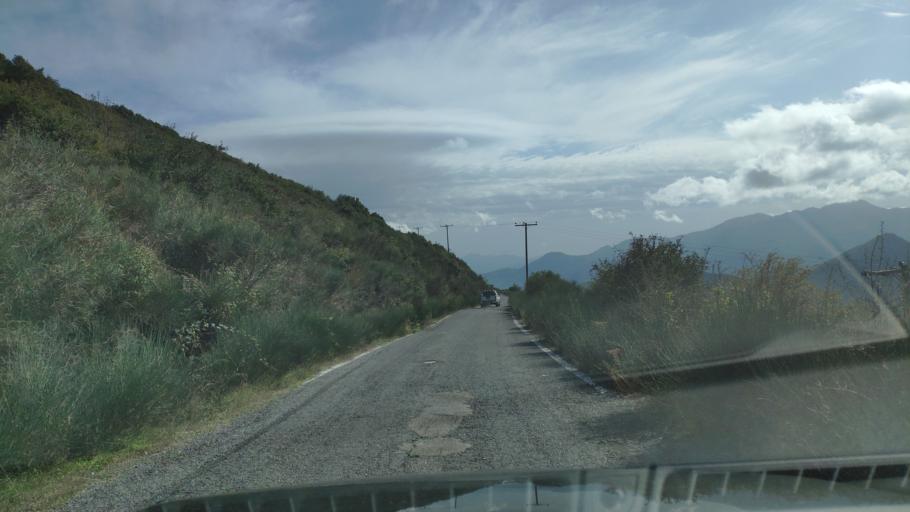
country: GR
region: Peloponnese
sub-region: Nomos Arkadias
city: Dimitsana
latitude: 37.5725
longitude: 22.0201
